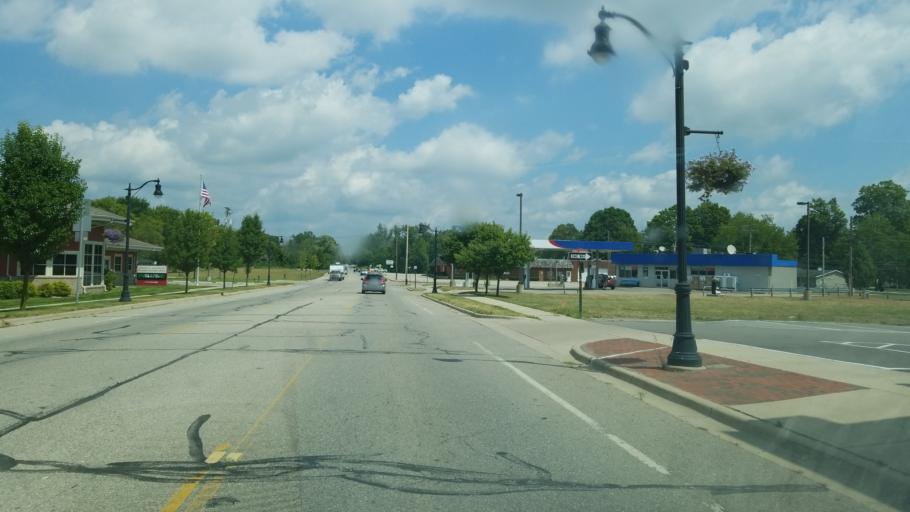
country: US
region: Michigan
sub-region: Montcalm County
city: Howard City
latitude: 43.3972
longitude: -85.4695
